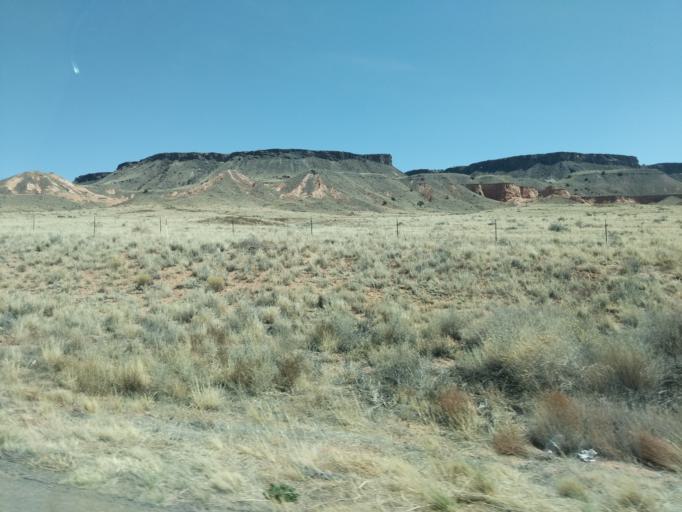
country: US
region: Arizona
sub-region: Navajo County
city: Dilkon
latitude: 35.4341
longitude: -110.0658
